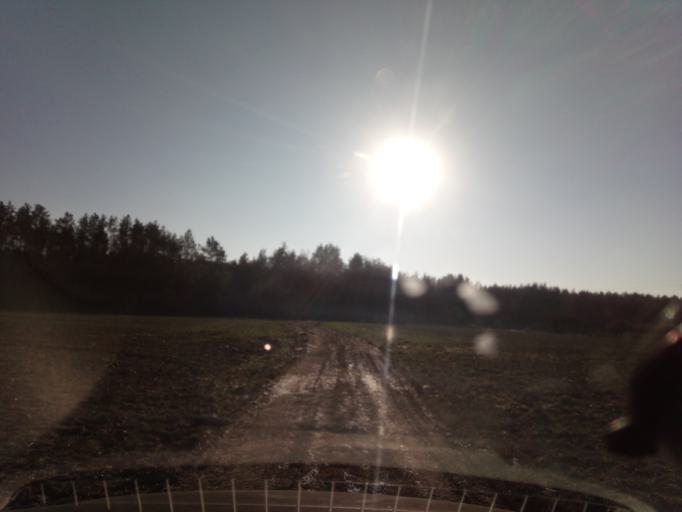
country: LT
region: Alytaus apskritis
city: Druskininkai
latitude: 53.9825
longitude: 23.8978
